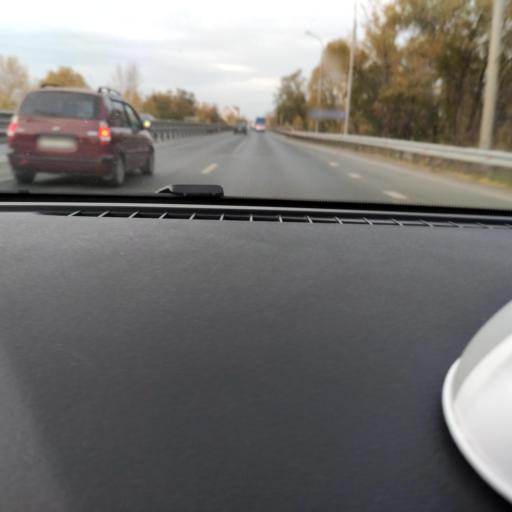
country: RU
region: Samara
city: Samara
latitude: 53.1037
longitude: 50.1624
